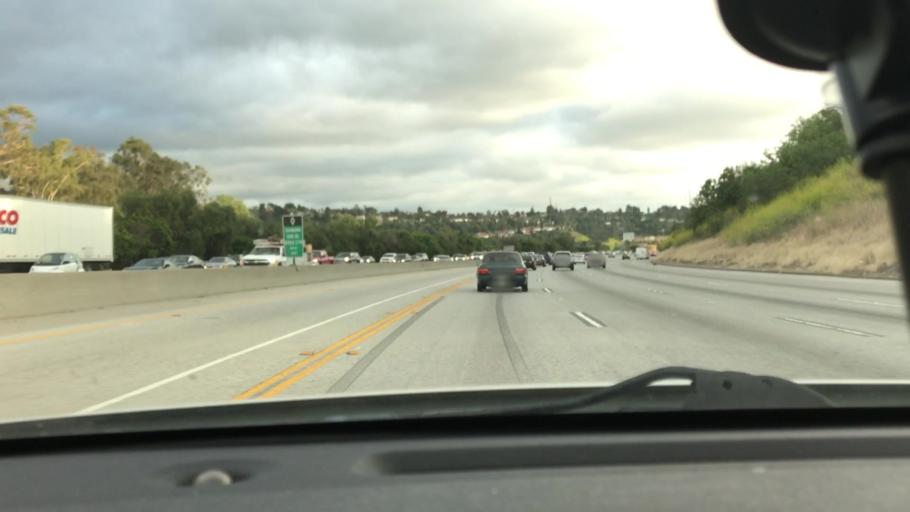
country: US
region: California
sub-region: Los Angeles County
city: Walnut
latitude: 33.9812
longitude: -117.8419
